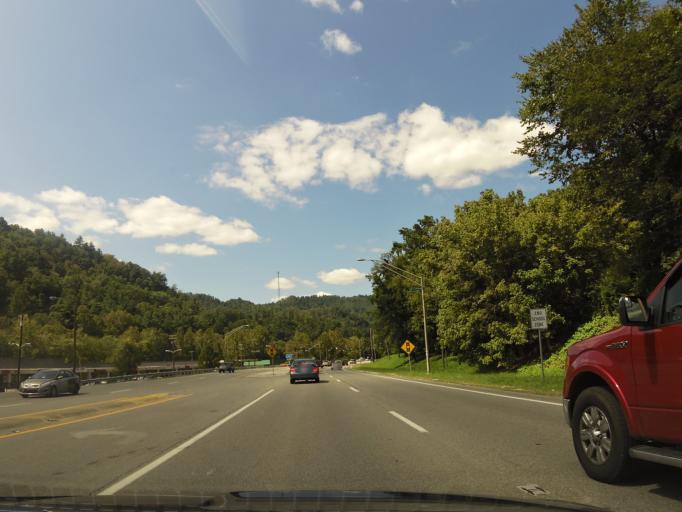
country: US
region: Kentucky
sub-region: Harlan County
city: Harlan
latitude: 36.8258
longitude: -83.3213
